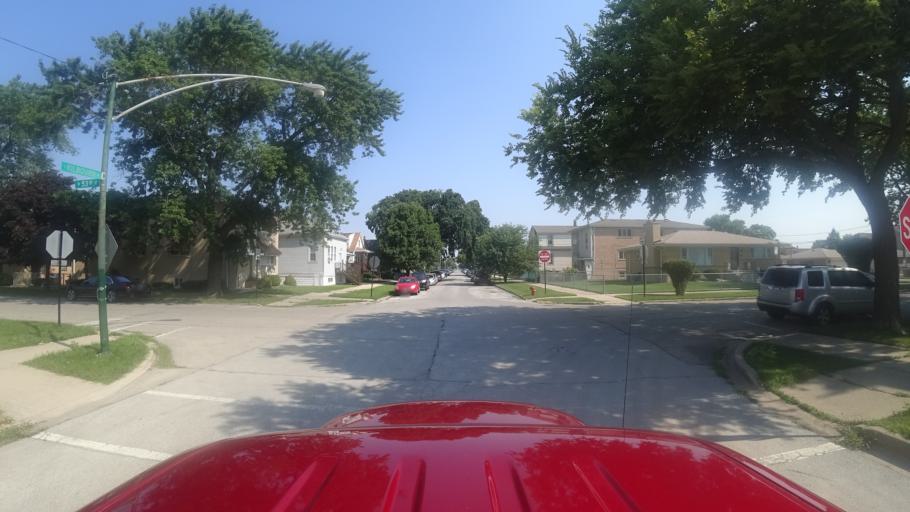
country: US
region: Illinois
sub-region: Cook County
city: Cicero
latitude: 41.7966
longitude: -87.7355
